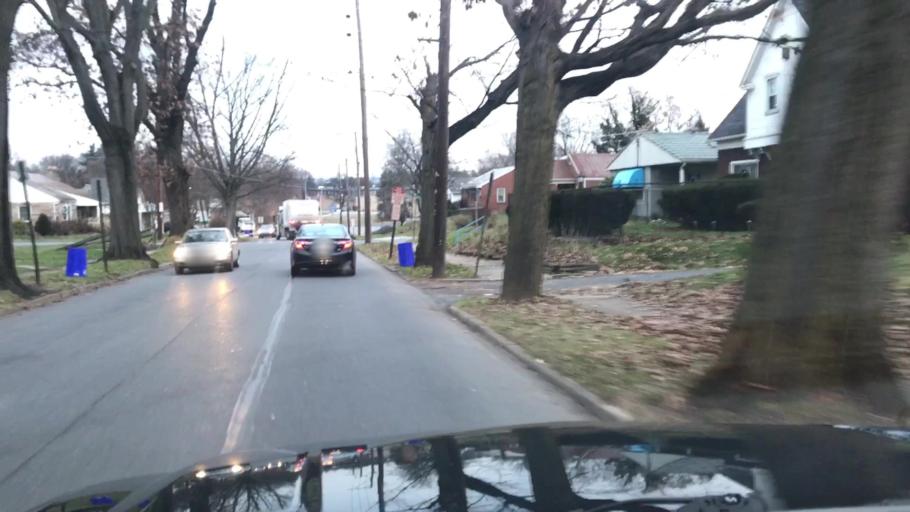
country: US
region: Pennsylvania
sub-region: Dauphin County
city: Harrisburg
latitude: 40.2767
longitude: -76.8692
